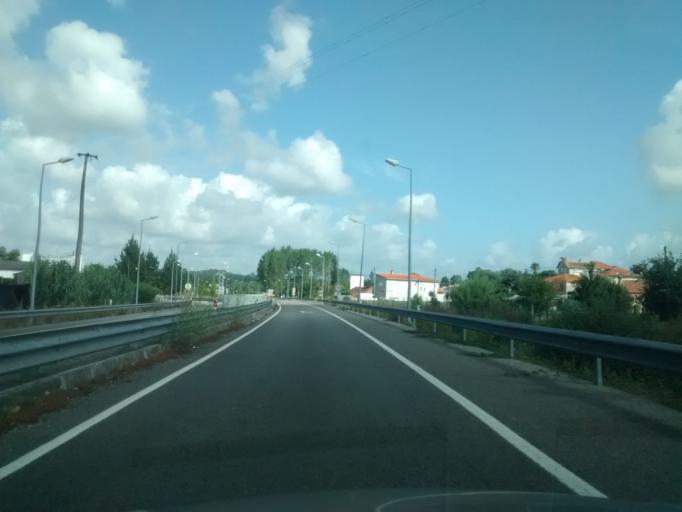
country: PT
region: Aveiro
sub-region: Anadia
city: Sangalhos
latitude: 40.4801
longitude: -8.4778
